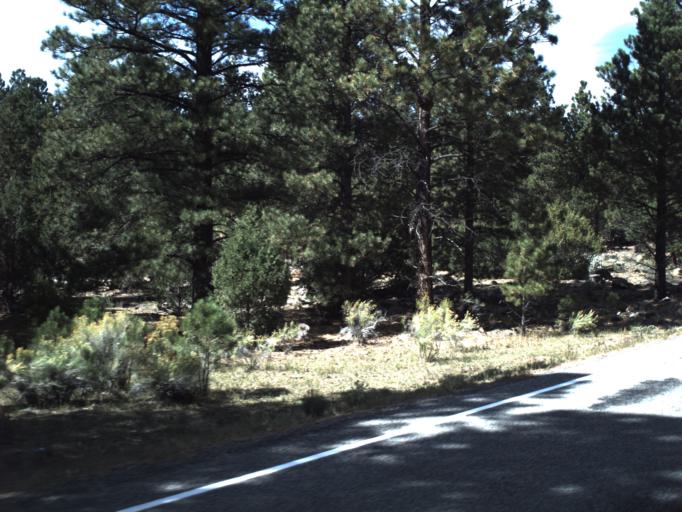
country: US
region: Utah
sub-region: Wayne County
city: Loa
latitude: 38.1651
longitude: -111.3366
